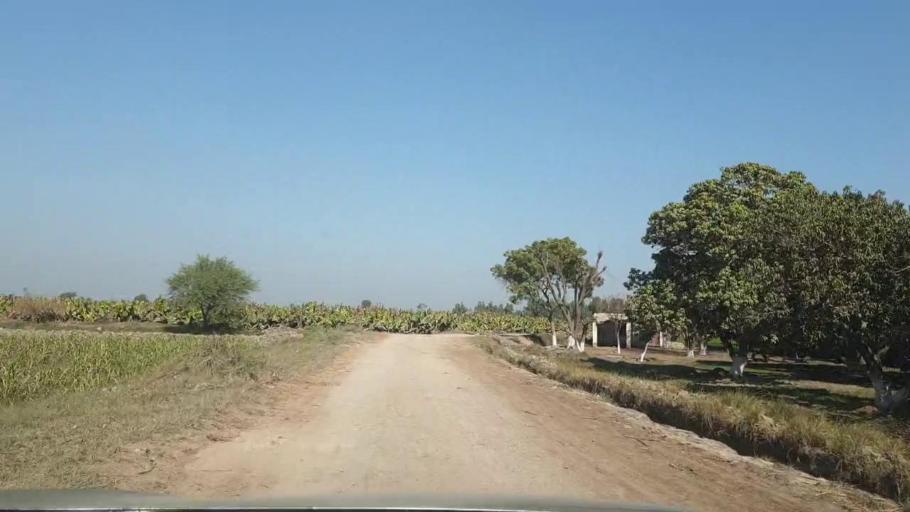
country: PK
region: Sindh
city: Tando Adam
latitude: 25.6237
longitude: 68.6441
